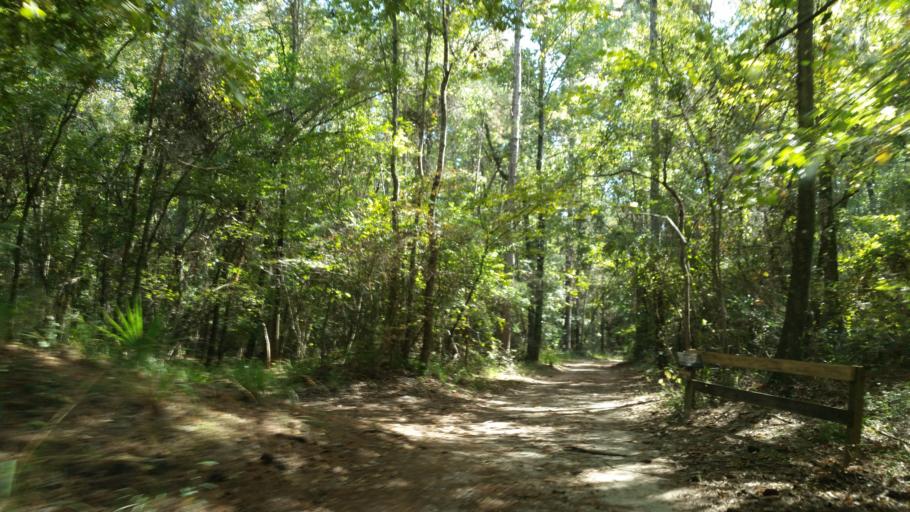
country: US
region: Alabama
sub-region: Baldwin County
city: Spanish Fort
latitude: 30.7395
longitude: -87.9195
